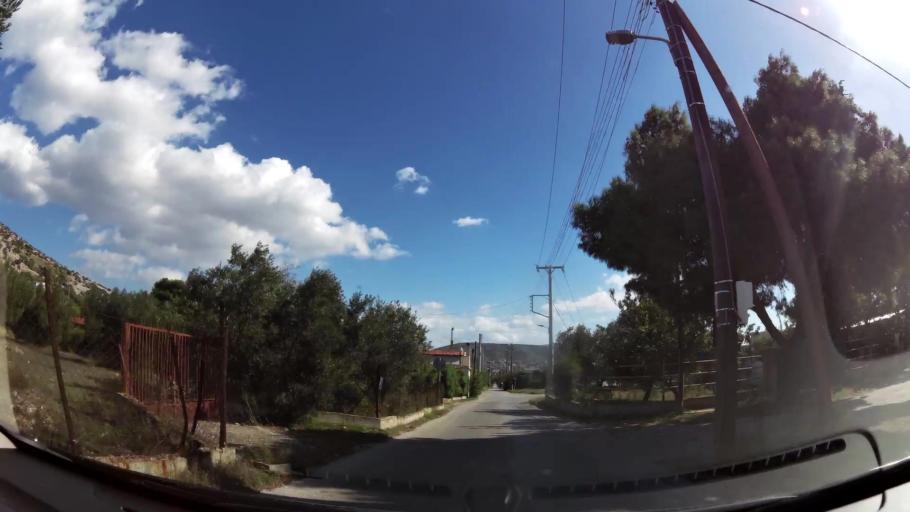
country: GR
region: Attica
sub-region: Nomarchia Anatolikis Attikis
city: Vari
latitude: 37.8414
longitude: 23.7994
